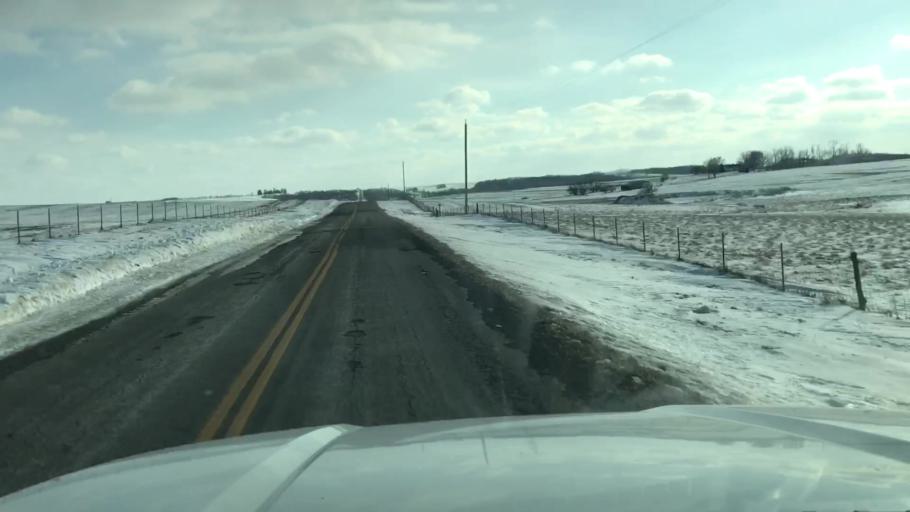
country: US
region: Missouri
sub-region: Nodaway County
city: Maryville
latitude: 40.1869
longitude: -95.0124
